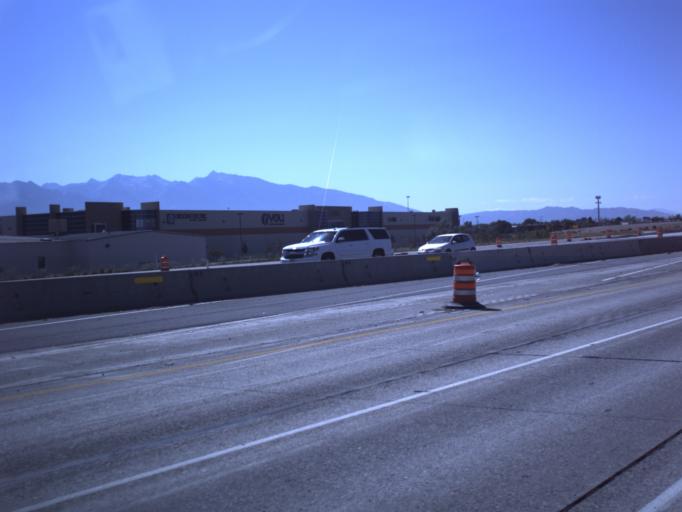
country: US
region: Utah
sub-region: Salt Lake County
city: South Salt Lake
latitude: 40.7304
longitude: -111.9503
